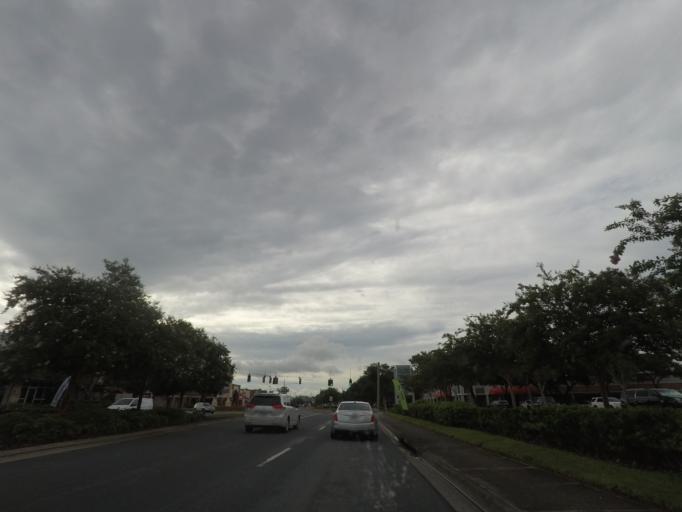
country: US
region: Florida
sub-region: Pinellas County
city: Seminole
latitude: 27.8409
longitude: -82.7943
